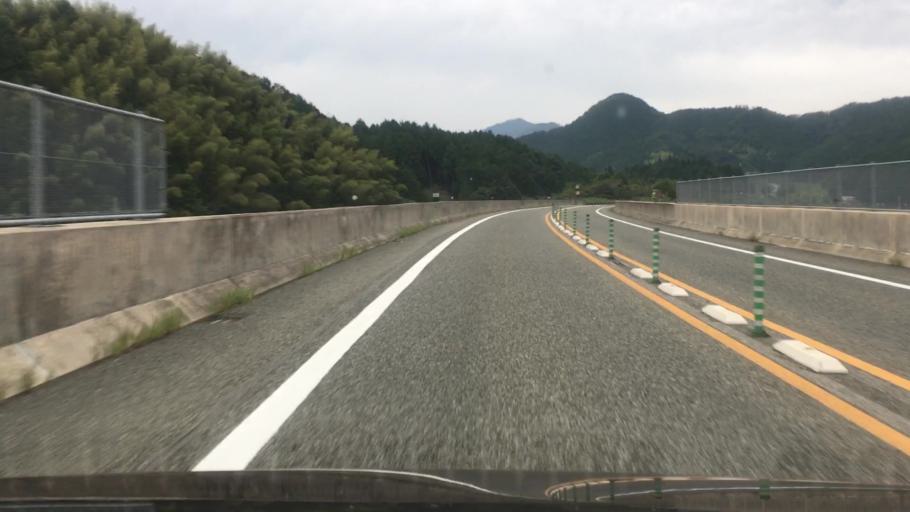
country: JP
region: Kyoto
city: Fukuchiyama
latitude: 35.3059
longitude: 134.8809
